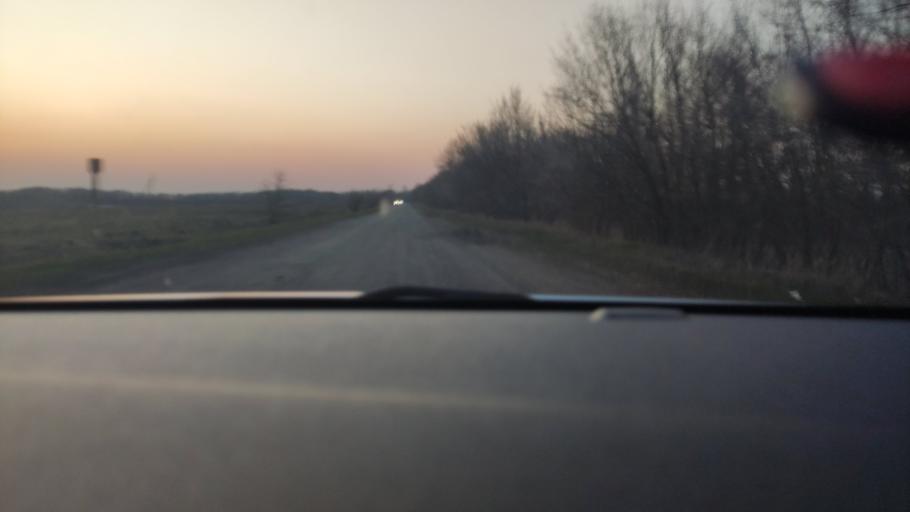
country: RU
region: Voronezj
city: Uryv-Pokrovka
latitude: 51.1169
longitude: 39.1420
